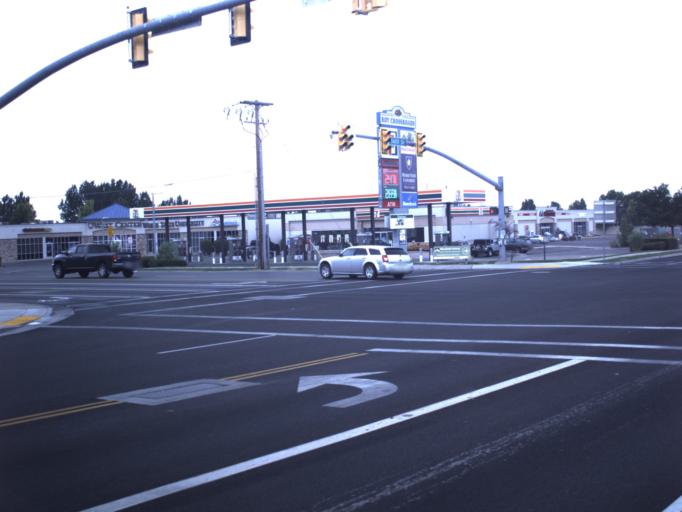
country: US
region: Utah
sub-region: Davis County
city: Clinton
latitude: 41.1616
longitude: -112.0641
